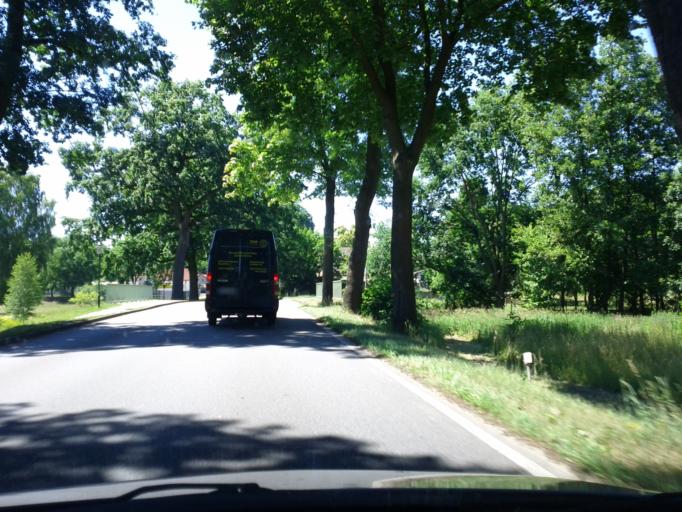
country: DE
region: Brandenburg
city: Rehfelde
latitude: 52.4808
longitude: 13.9015
